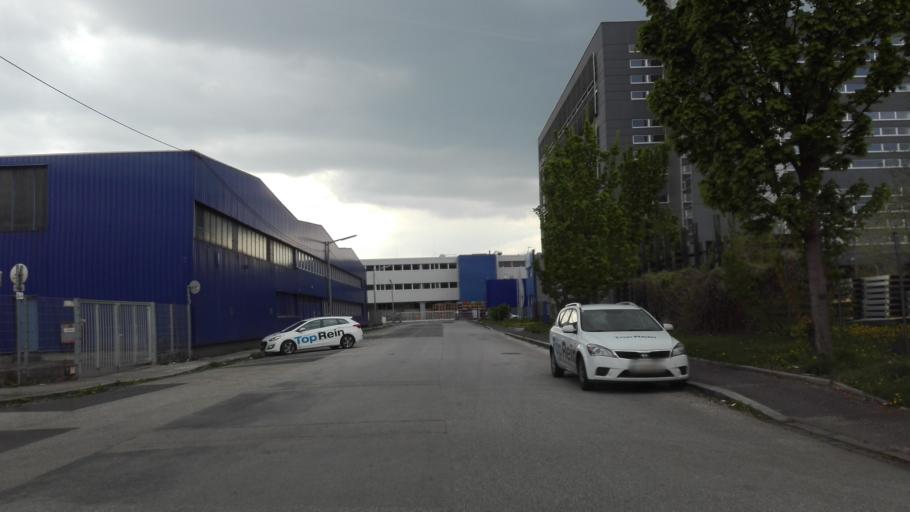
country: AT
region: Upper Austria
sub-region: Linz Stadt
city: Linz
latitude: 48.3083
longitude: 14.3205
